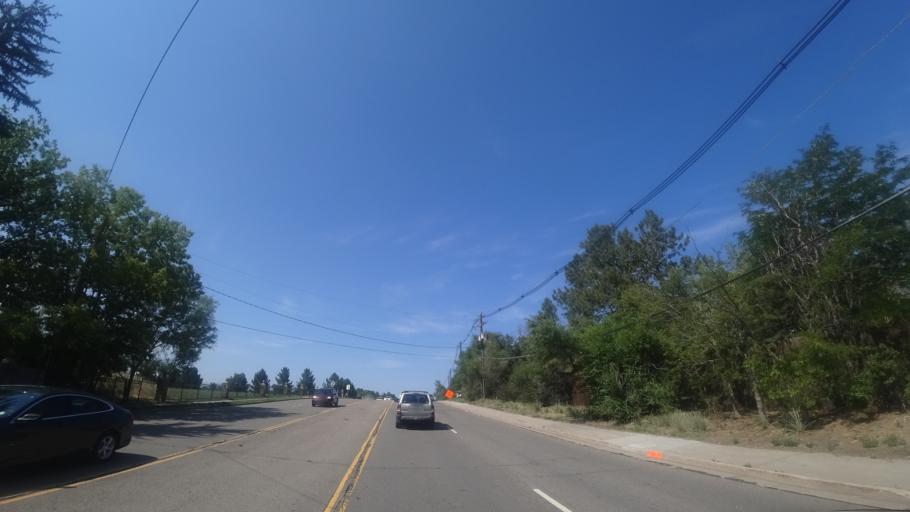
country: US
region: Colorado
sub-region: Arapahoe County
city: Cherry Hills Village
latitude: 39.6402
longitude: -104.9597
